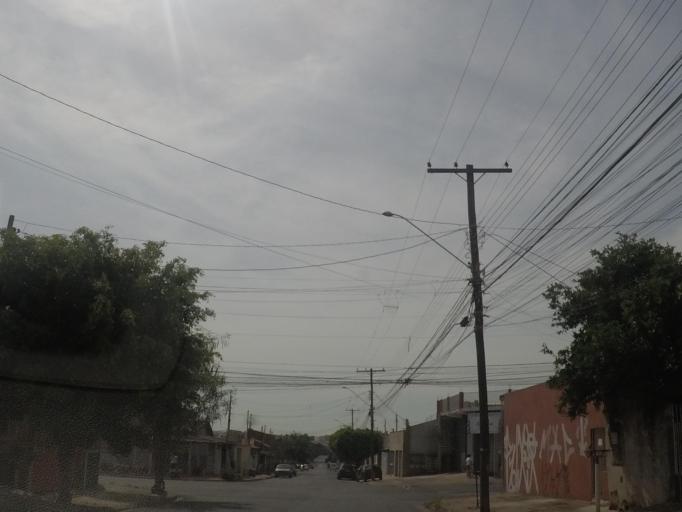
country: BR
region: Sao Paulo
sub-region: Hortolandia
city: Hortolandia
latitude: -22.8483
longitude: -47.1969
